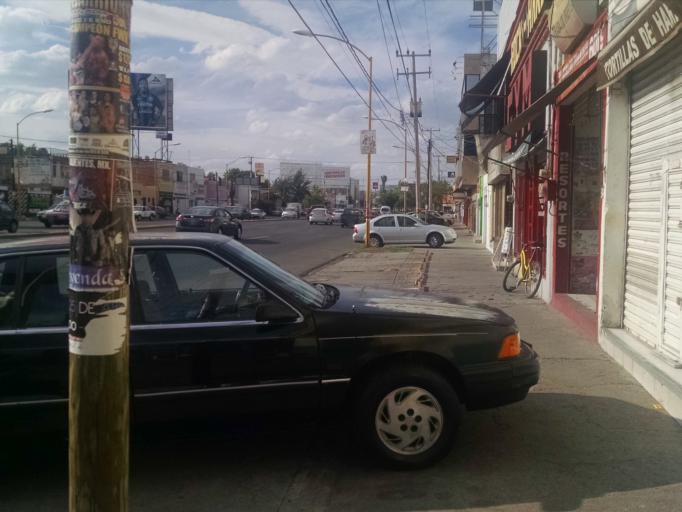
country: MX
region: Aguascalientes
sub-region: Aguascalientes
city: Aguascalientes
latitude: 21.8796
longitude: -102.3123
